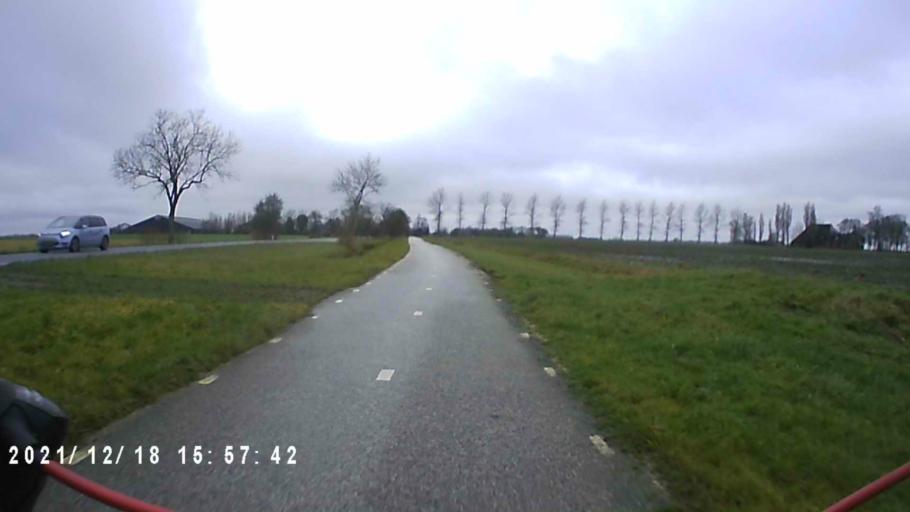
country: NL
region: Friesland
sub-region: Gemeente Dongeradeel
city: Anjum
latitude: 53.3353
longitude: 6.0946
